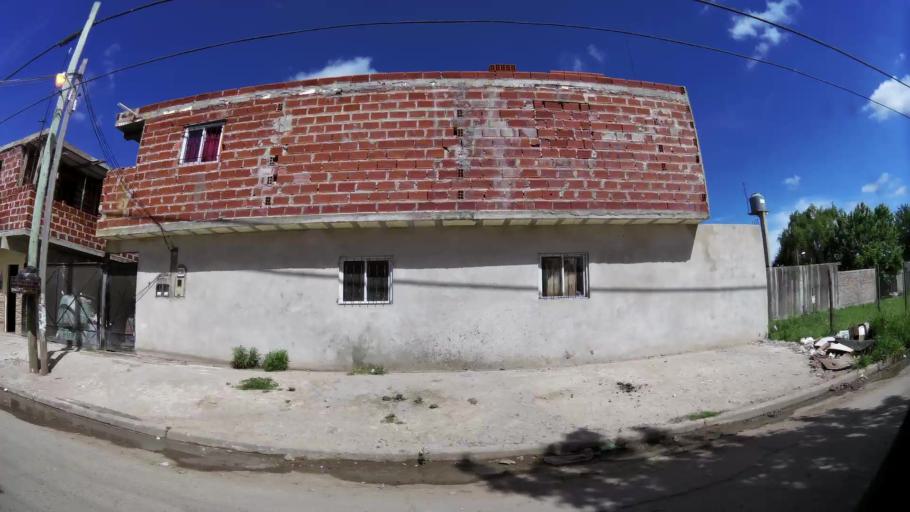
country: AR
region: Buenos Aires
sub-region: Partido de Quilmes
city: Quilmes
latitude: -34.8227
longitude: -58.2595
